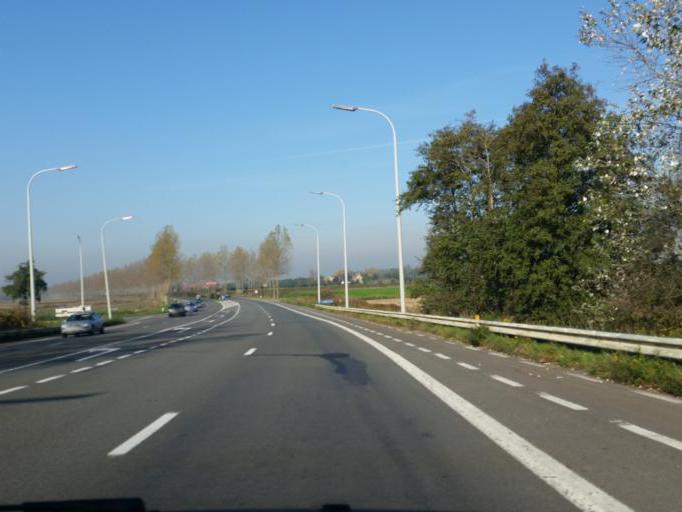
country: BE
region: Flanders
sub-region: Provincie West-Vlaanderen
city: Jabbeke
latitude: 51.2061
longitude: 3.0927
